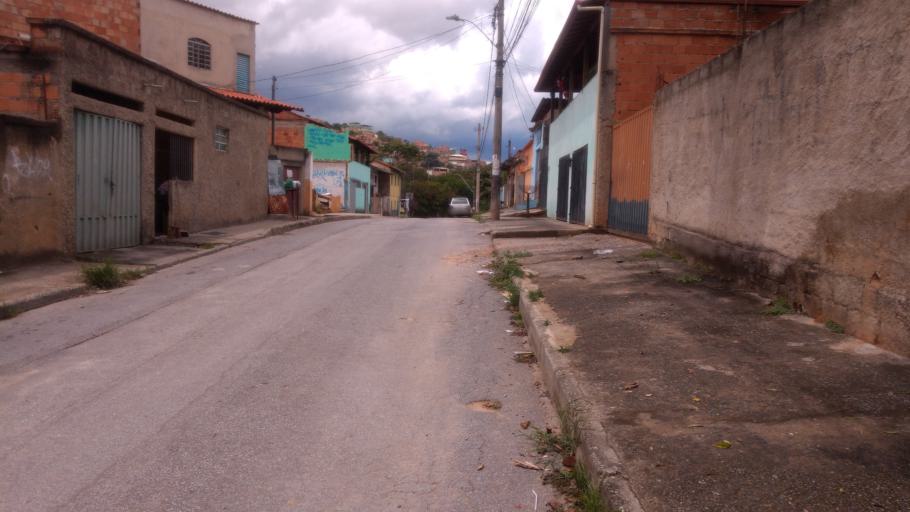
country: BR
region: Minas Gerais
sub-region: Santa Luzia
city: Santa Luzia
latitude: -19.8361
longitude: -43.9064
